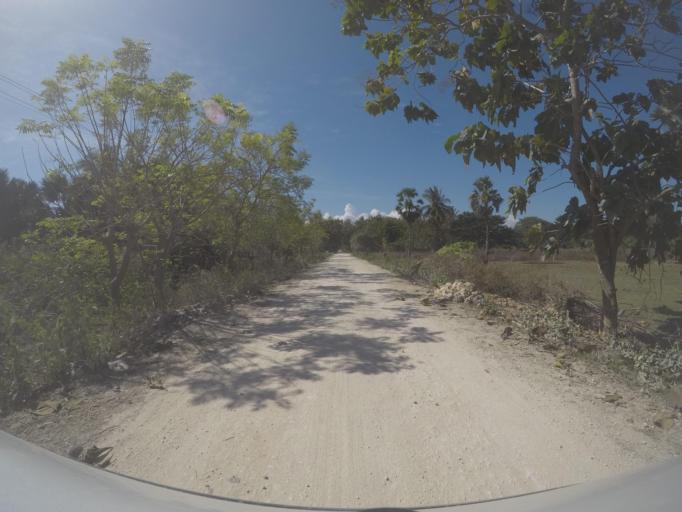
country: TL
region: Viqueque
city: Viqueque
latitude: -8.8875
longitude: 126.5070
